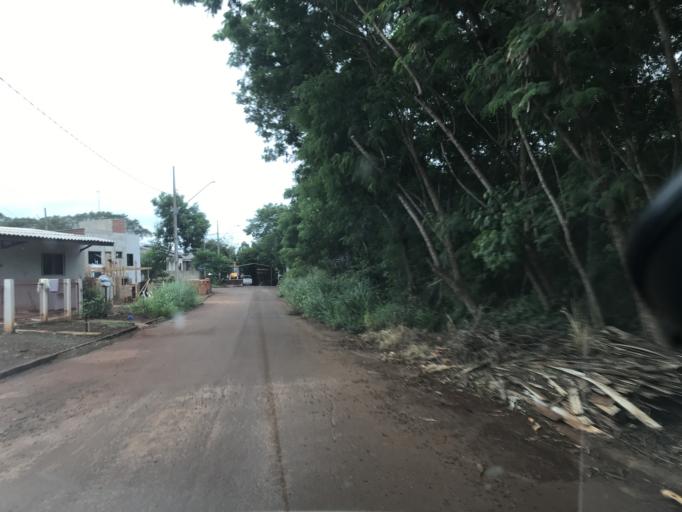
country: BR
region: Parana
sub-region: Palotina
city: Palotina
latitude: -24.2994
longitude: -53.8280
